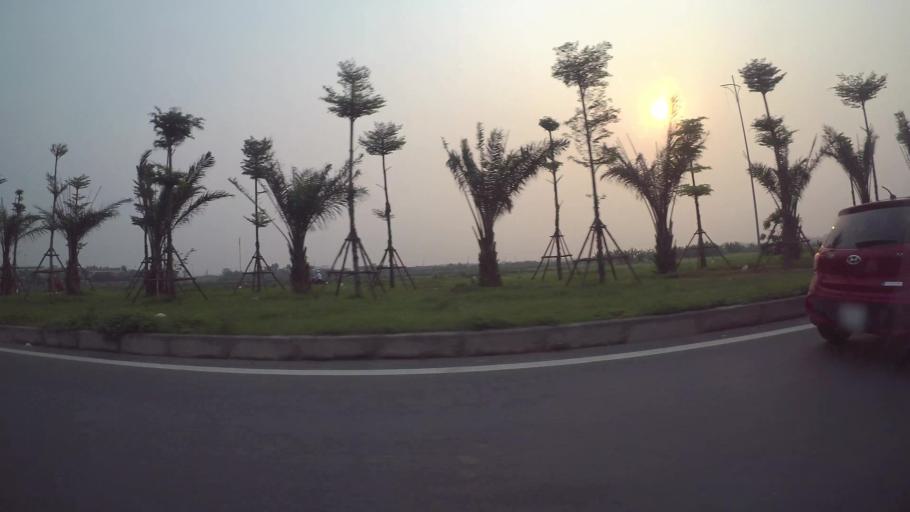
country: VN
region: Ha Noi
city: Kim Bai
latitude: 20.8757
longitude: 105.8019
